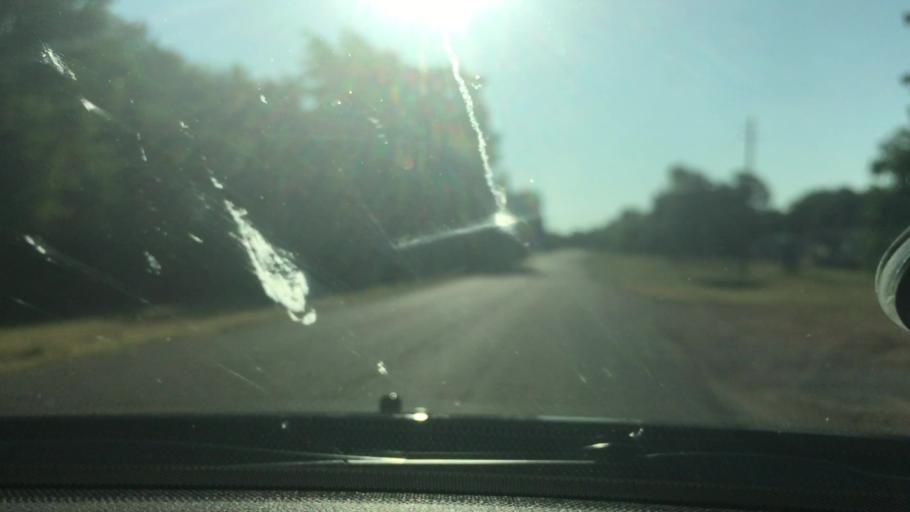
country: US
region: Oklahoma
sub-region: Murray County
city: Sulphur
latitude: 34.4041
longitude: -96.8242
